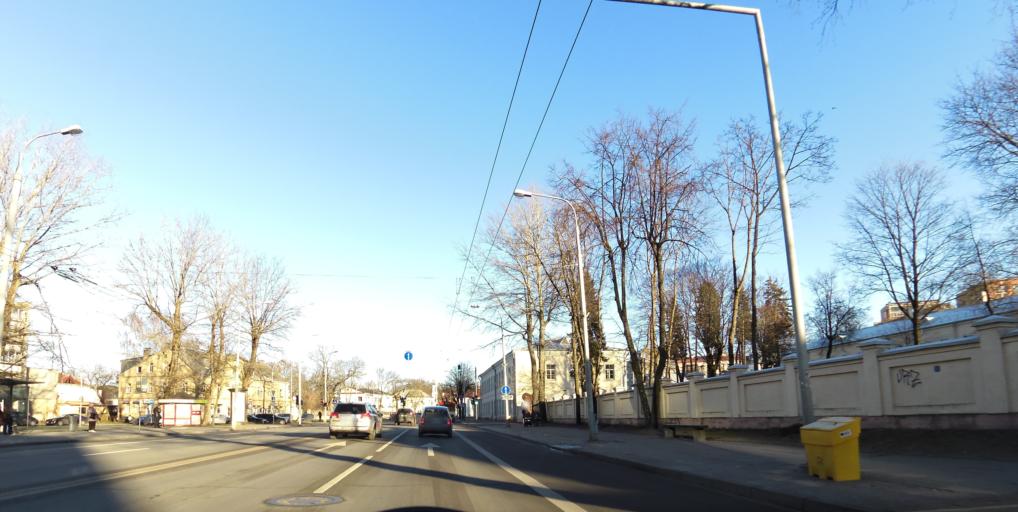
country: LT
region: Vilnius County
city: Naujamiestis
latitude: 54.6795
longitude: 25.2593
